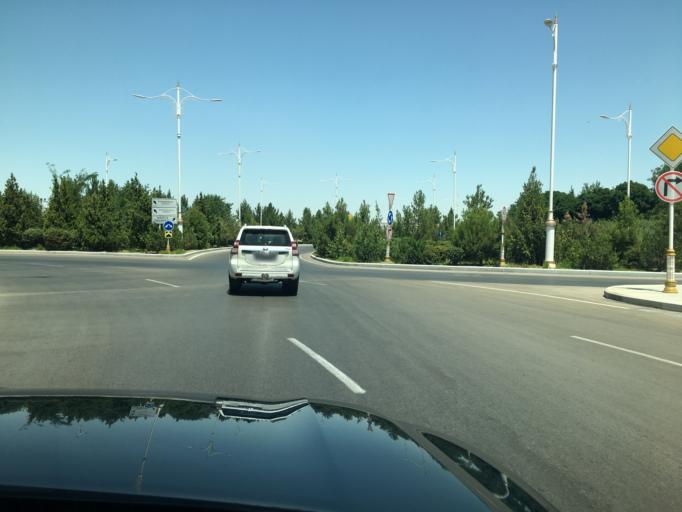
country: TM
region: Ahal
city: Ashgabat
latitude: 37.8790
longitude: 58.3876
